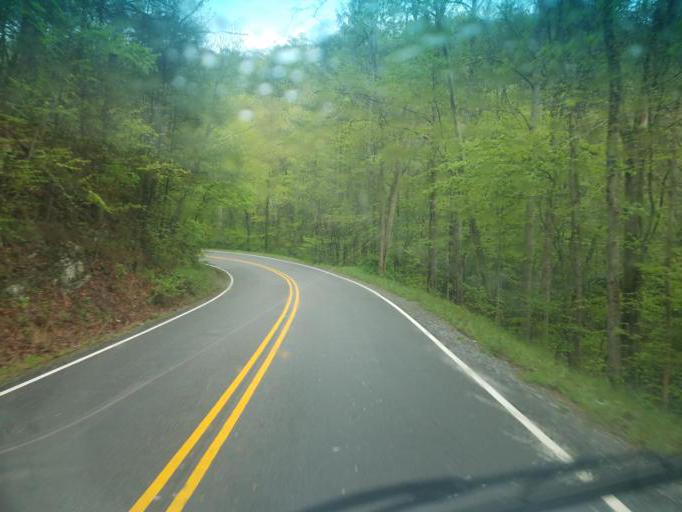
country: US
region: Tennessee
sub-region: Johnson County
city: Mountain City
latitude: 36.6257
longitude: -81.7569
